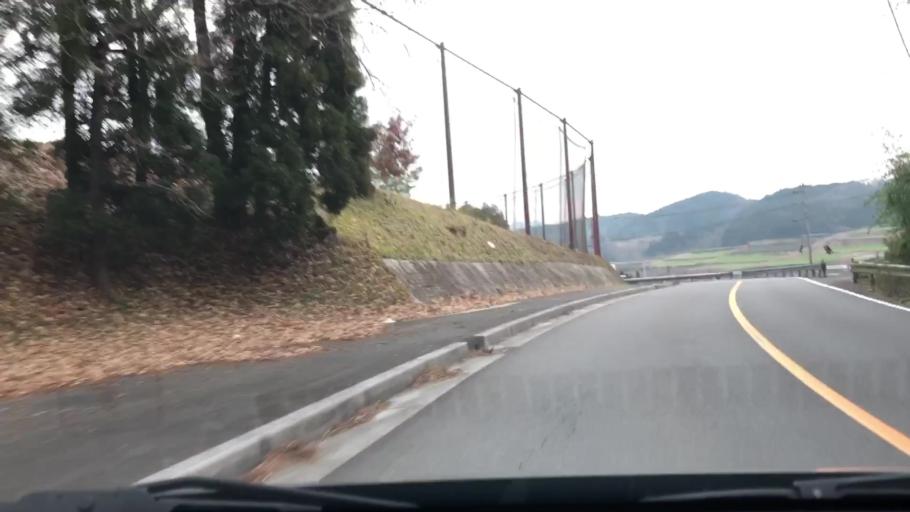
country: JP
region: Oita
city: Usuki
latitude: 33.0048
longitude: 131.6284
